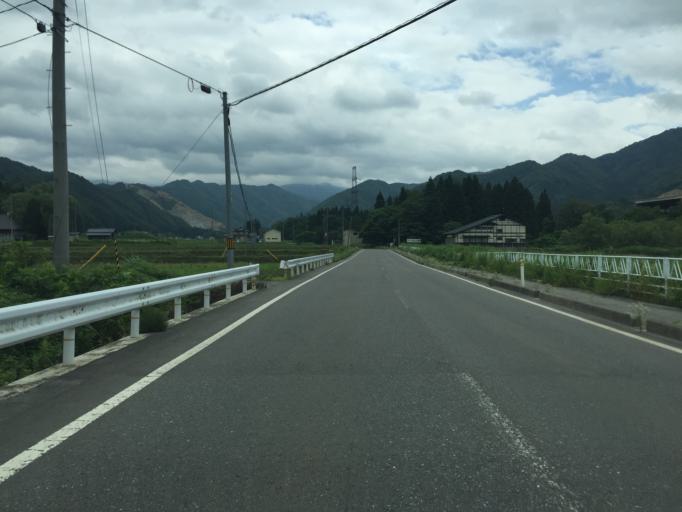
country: JP
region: Yamagata
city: Yonezawa
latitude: 37.8415
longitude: 140.0917
